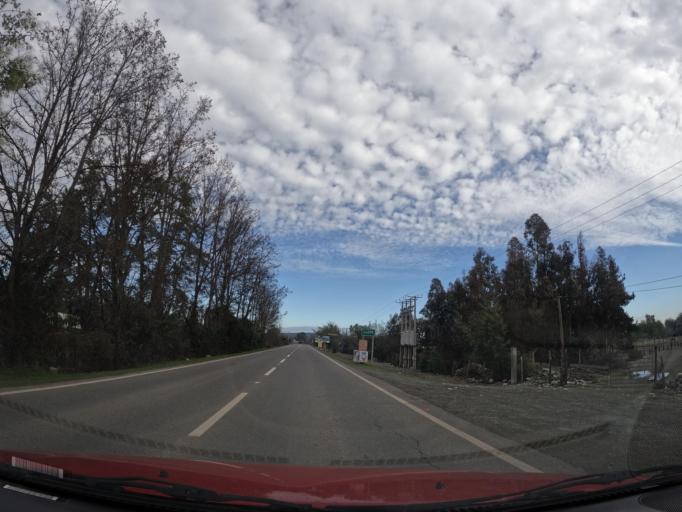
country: CL
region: Maule
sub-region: Provincia de Linares
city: Linares
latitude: -35.9107
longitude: -71.4922
